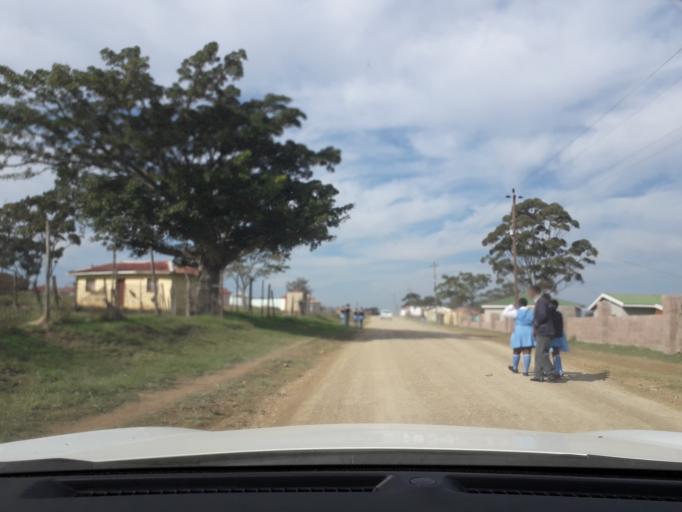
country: ZA
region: Eastern Cape
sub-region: Buffalo City Metropolitan Municipality
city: Bhisho
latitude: -33.0000
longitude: 27.3311
